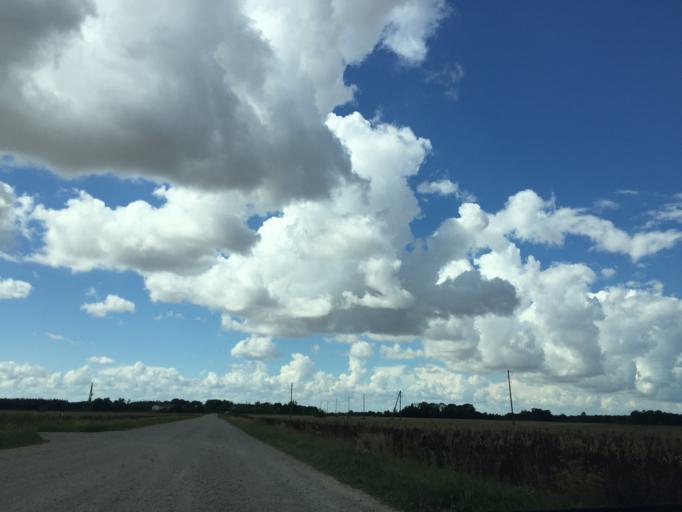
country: LV
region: Rundales
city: Pilsrundale
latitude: 56.3629
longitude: 24.0322
